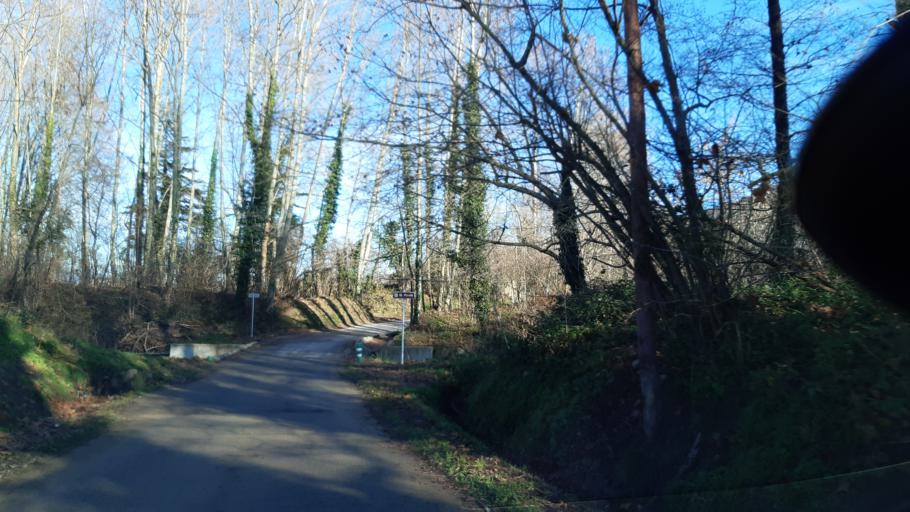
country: ES
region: Catalonia
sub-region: Provincia de Girona
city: Bas
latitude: 42.1432
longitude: 2.4498
